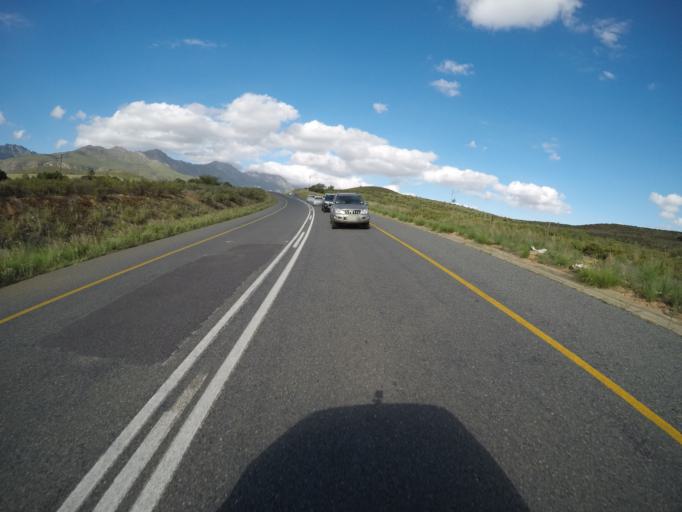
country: ZA
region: Western Cape
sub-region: Cape Winelands District Municipality
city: Ashton
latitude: -33.9497
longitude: 20.2215
